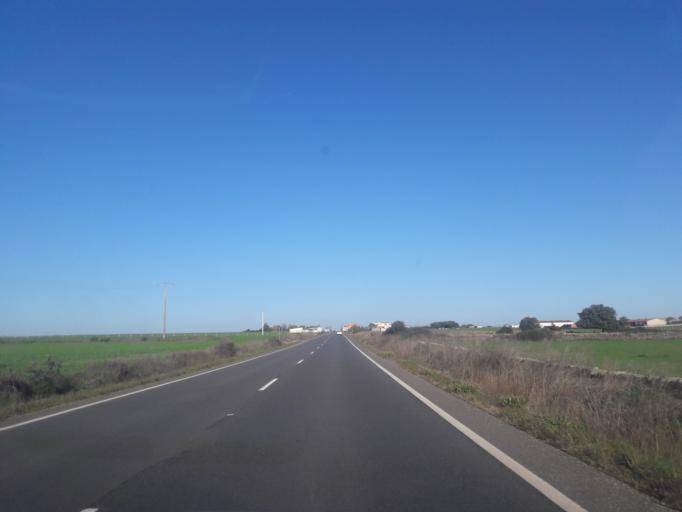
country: ES
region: Castille and Leon
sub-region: Provincia de Salamanca
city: Villarmayor
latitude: 41.0109
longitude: -5.9636
